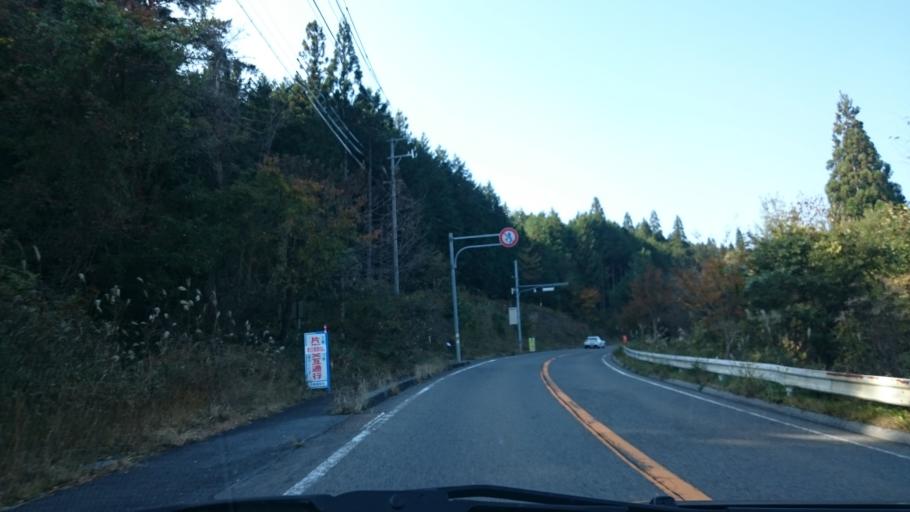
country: JP
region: Gifu
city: Nakatsugawa
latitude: 35.7451
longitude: 137.3317
